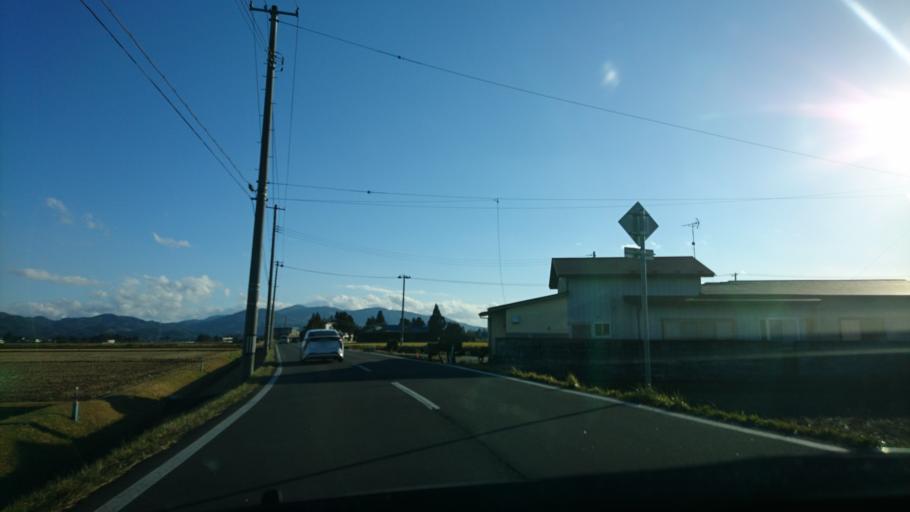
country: JP
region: Iwate
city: Mizusawa
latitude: 39.0978
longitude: 141.1587
